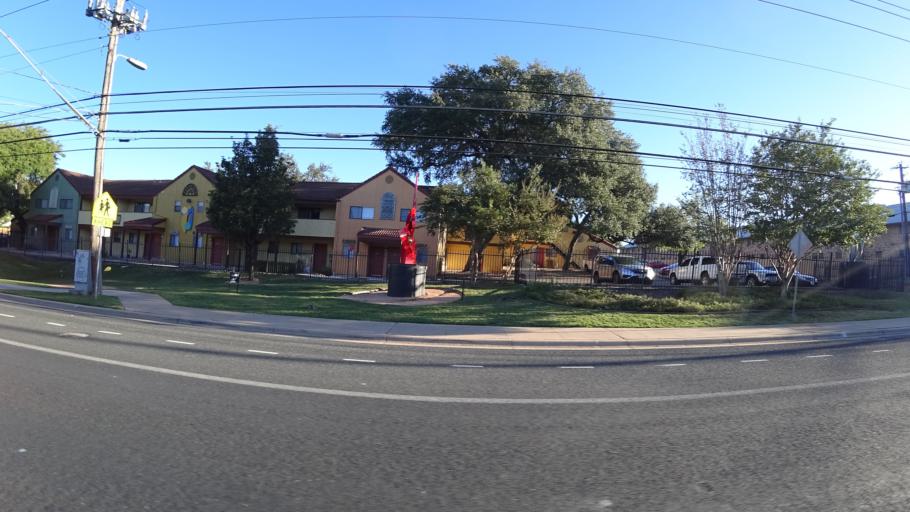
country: US
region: Texas
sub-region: Travis County
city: Austin
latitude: 30.2200
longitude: -97.7706
